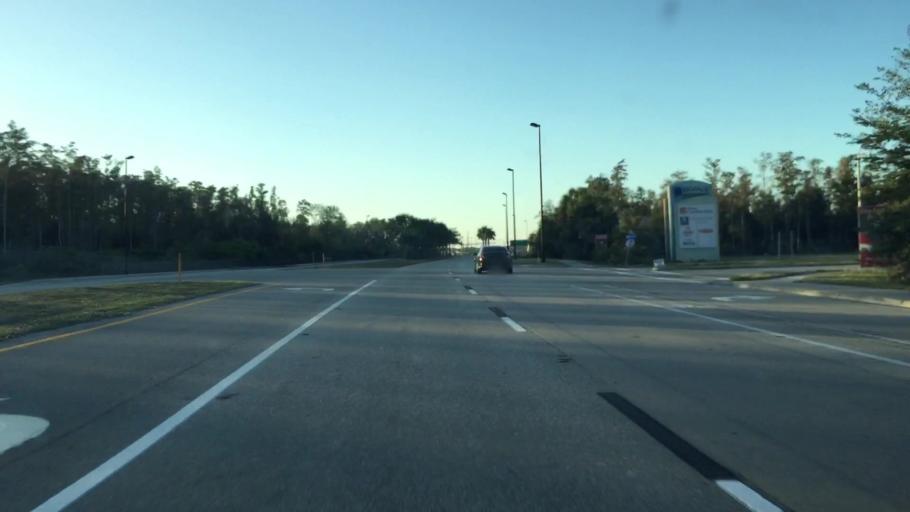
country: US
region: Florida
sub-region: Lee County
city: Three Oaks
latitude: 26.4978
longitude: -81.7839
